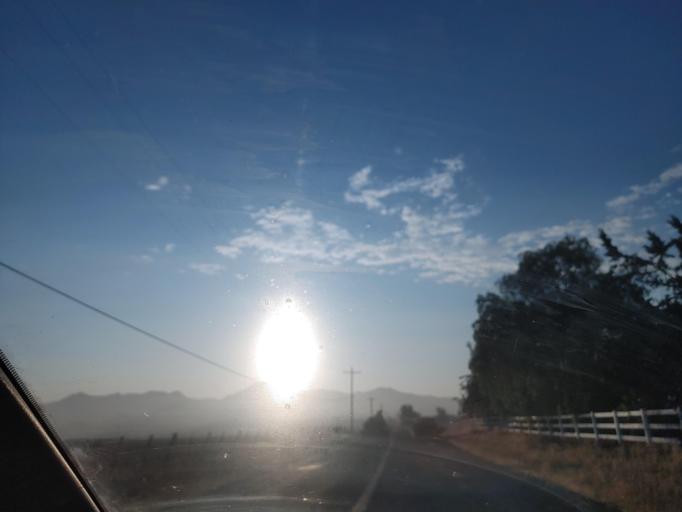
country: US
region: California
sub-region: San Benito County
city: Ridgemark
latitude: 36.8610
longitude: -121.3501
